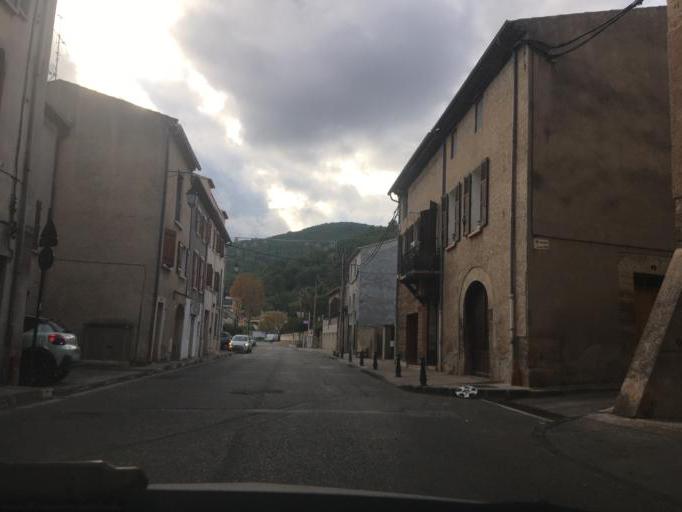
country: FR
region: Provence-Alpes-Cote d'Azur
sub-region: Departement du Var
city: Cuers
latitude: 43.2357
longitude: 6.0713
